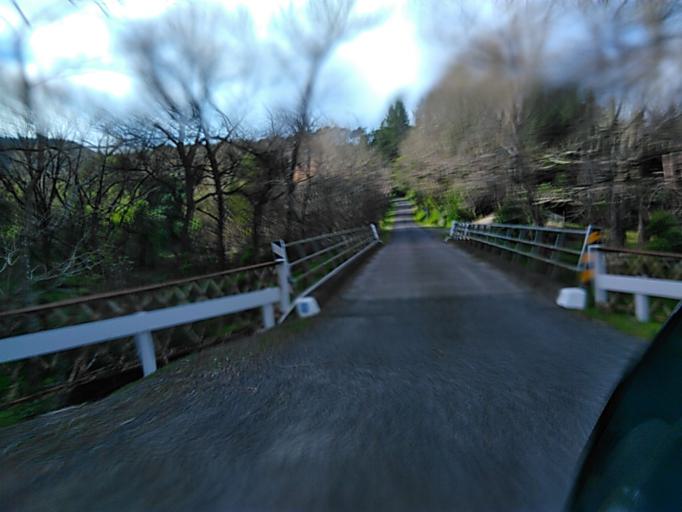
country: NZ
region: Gisborne
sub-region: Gisborne District
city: Gisborne
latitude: -38.6301
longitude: 178.0528
